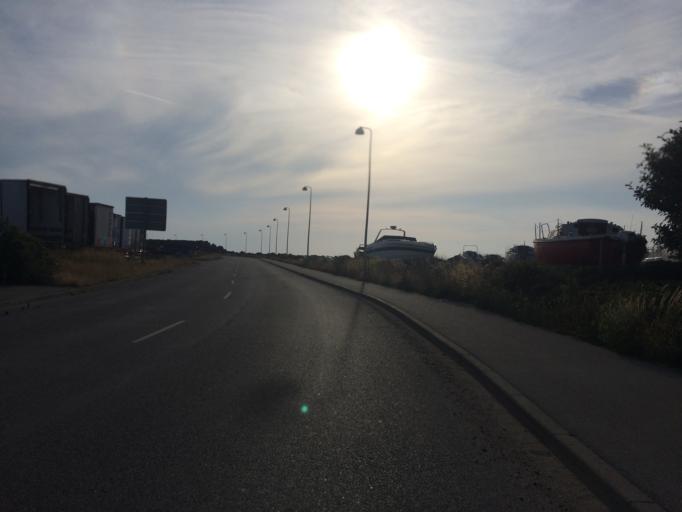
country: DK
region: Capital Region
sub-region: Bornholm Kommune
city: Ronne
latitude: 55.1031
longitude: 14.6910
